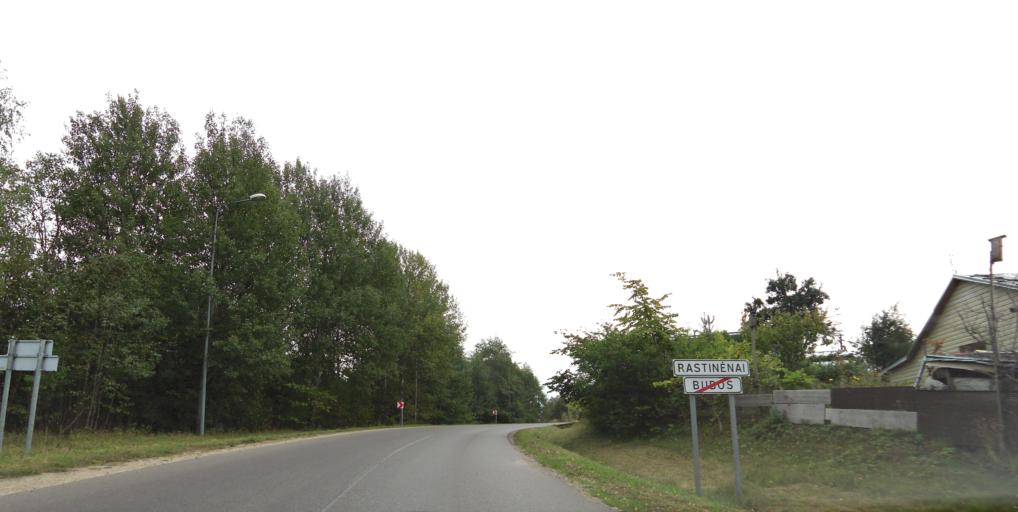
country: LT
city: Grigiskes
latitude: 54.7651
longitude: 25.0378
